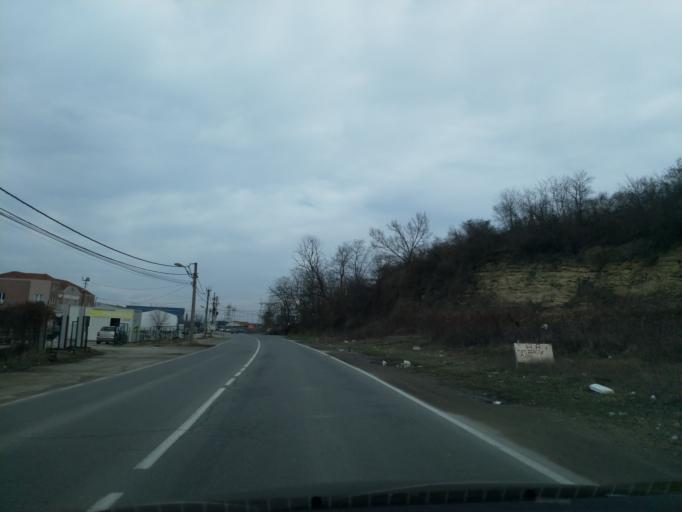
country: RS
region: Central Serbia
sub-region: Belgrade
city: Zvezdara
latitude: 44.7294
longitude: 20.5828
